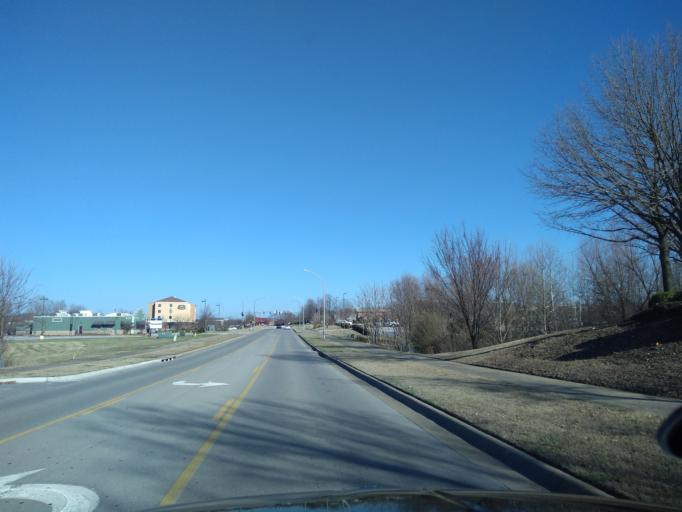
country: US
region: Arkansas
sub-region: Washington County
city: Johnson
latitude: 36.1176
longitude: -94.1527
